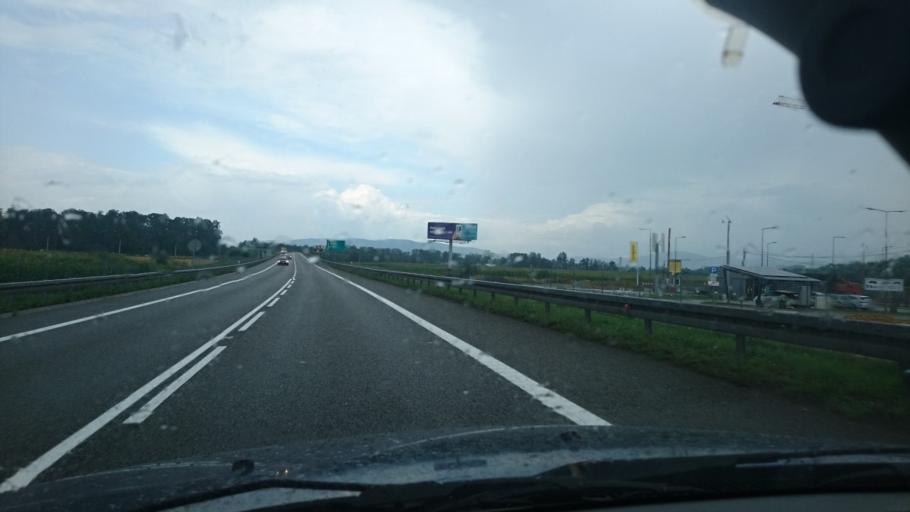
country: PL
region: Silesian Voivodeship
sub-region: Powiat zywiecki
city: Wieprz
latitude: 49.6508
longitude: 19.1715
